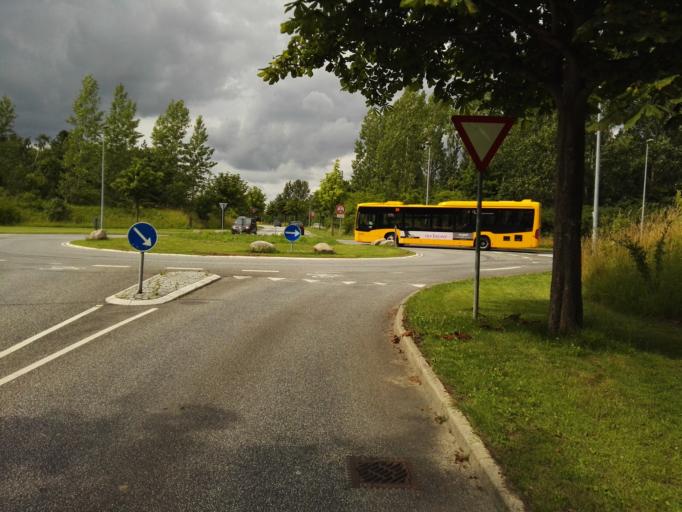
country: DK
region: Capital Region
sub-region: Egedal Kommune
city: Olstykke
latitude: 55.7870
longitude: 12.1693
